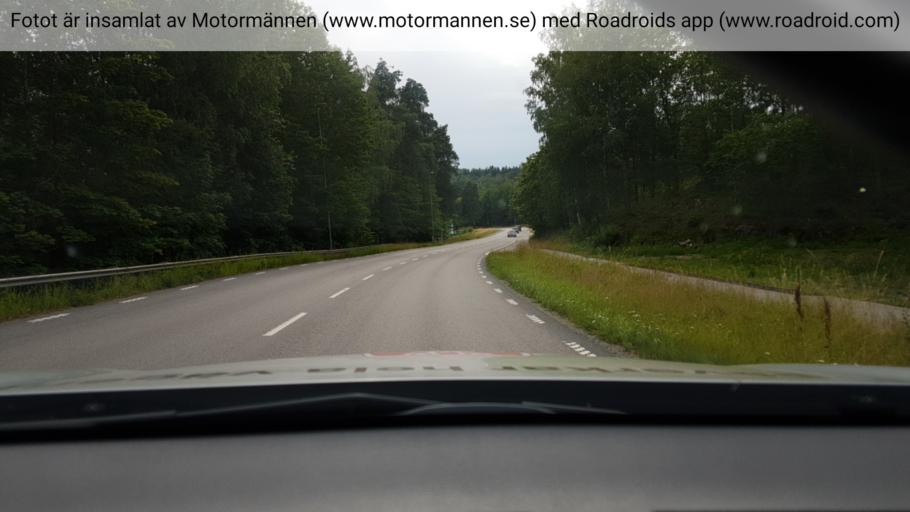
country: SE
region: Vaestra Goetaland
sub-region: Bengtsfors Kommun
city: Billingsfors
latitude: 58.9906
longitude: 12.2633
